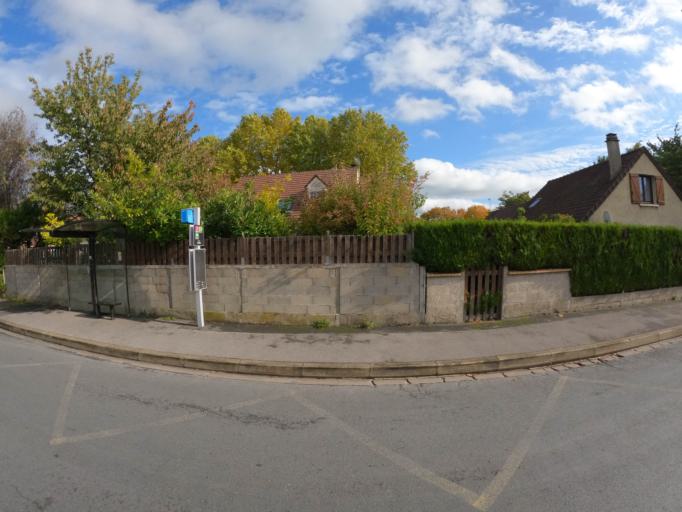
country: FR
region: Ile-de-France
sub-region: Departement de Seine-et-Marne
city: Chelles
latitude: 48.8898
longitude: 2.6042
